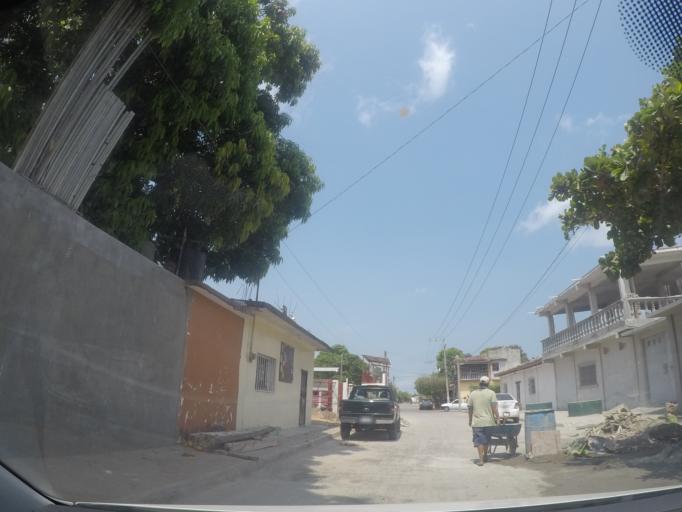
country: MX
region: Oaxaca
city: Asuncion Ixtaltepec
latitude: 16.5032
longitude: -95.0580
